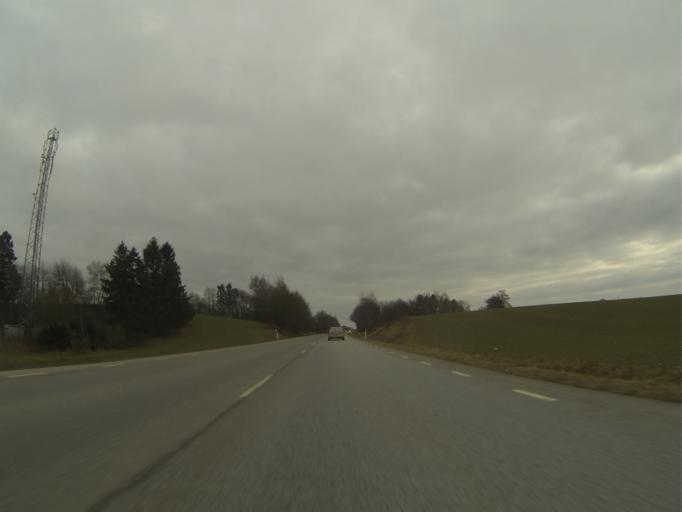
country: SE
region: Skane
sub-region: Svedala Kommun
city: Svedala
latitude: 55.5230
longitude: 13.2068
